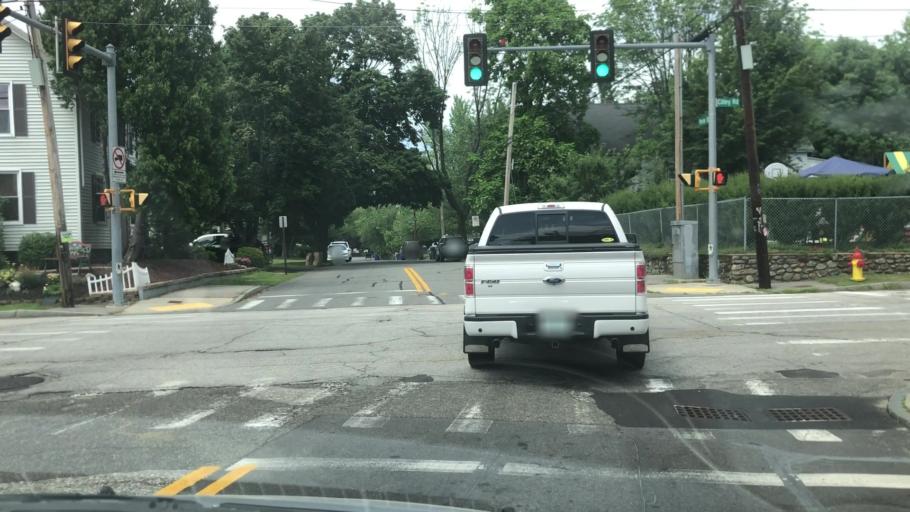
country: US
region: New Hampshire
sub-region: Hillsborough County
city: Manchester
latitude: 42.9733
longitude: -71.4323
